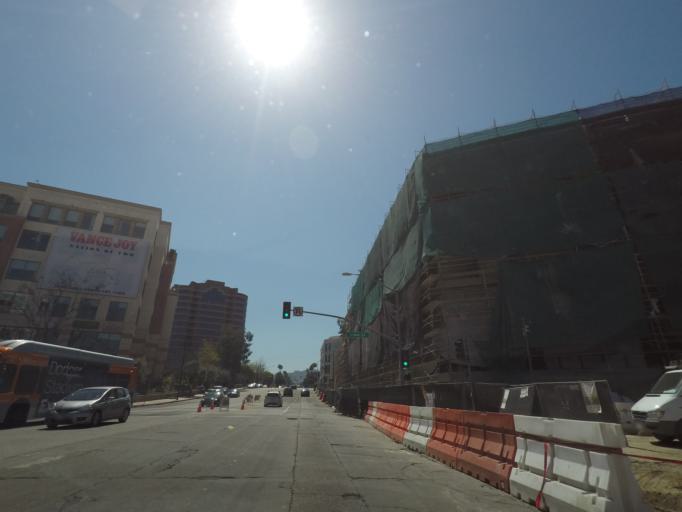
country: US
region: California
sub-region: Los Angeles County
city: Universal City
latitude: 34.1544
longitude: -118.3367
